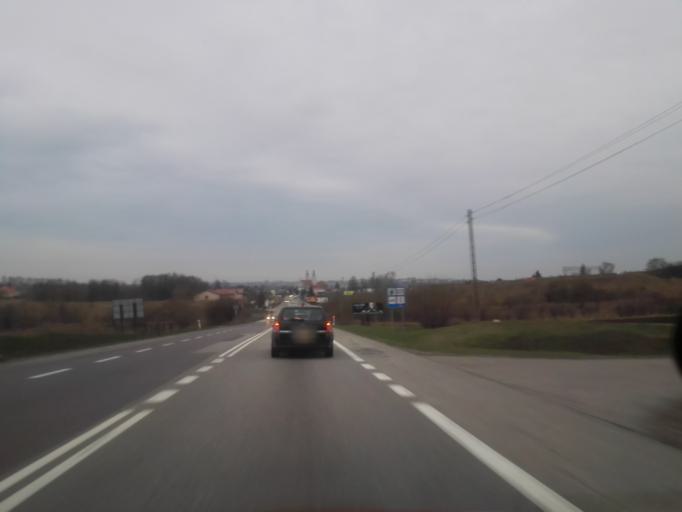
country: PL
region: Podlasie
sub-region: Powiat lomzynski
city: Piatnica
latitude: 53.2047
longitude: 22.1016
